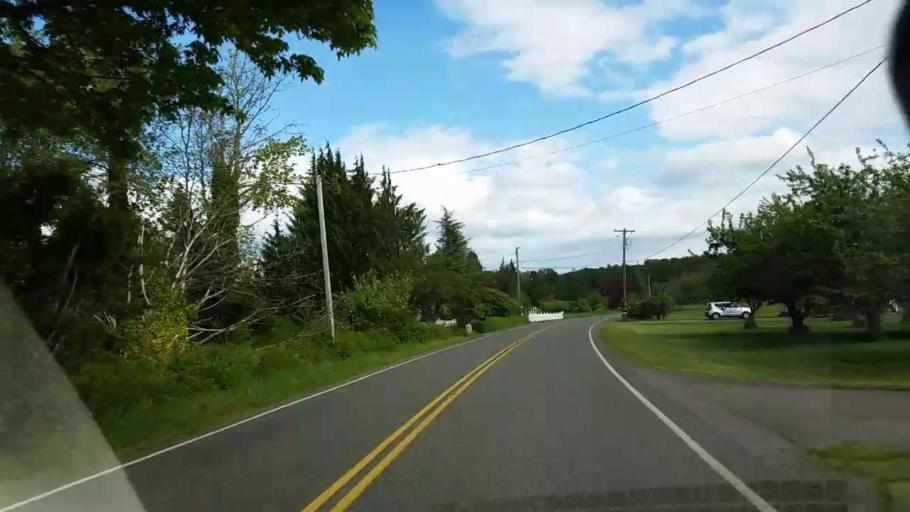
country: US
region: Washington
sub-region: Mason County
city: Shelton
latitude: 47.3196
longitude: -123.2626
